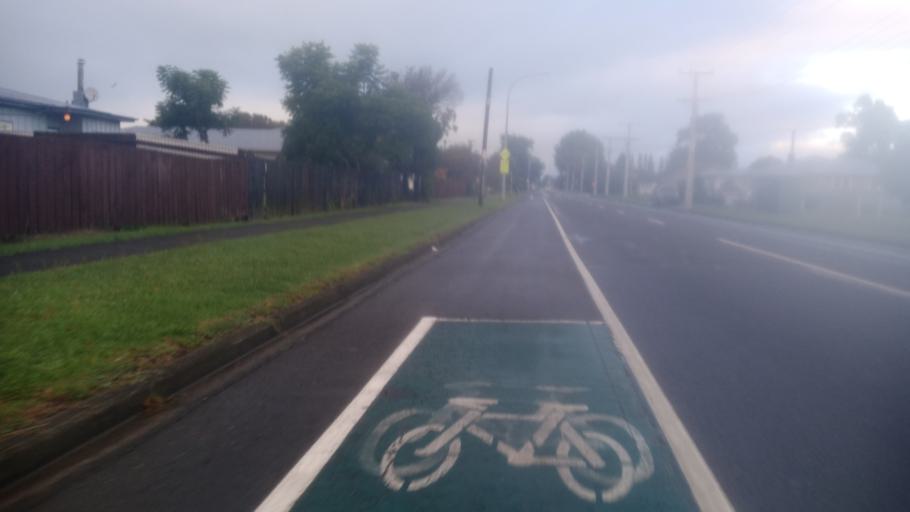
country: NZ
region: Gisborne
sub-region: Gisborne District
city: Gisborne
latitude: -38.6545
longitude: 177.9968
